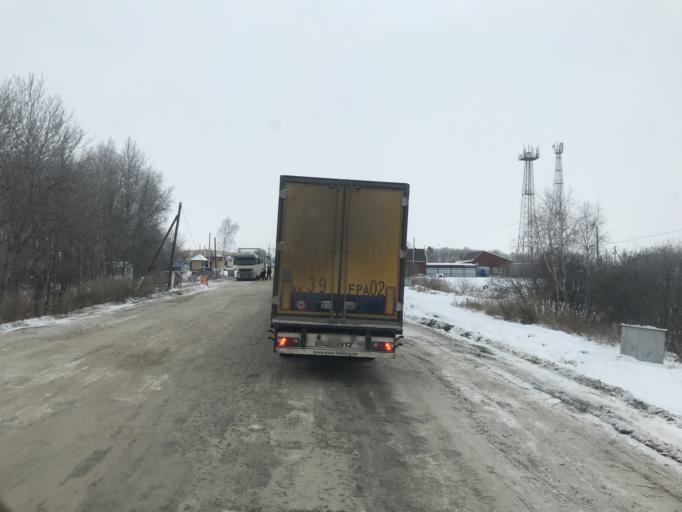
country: RU
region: Kurgan
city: Petukhovo
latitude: 55.0942
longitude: 68.2811
